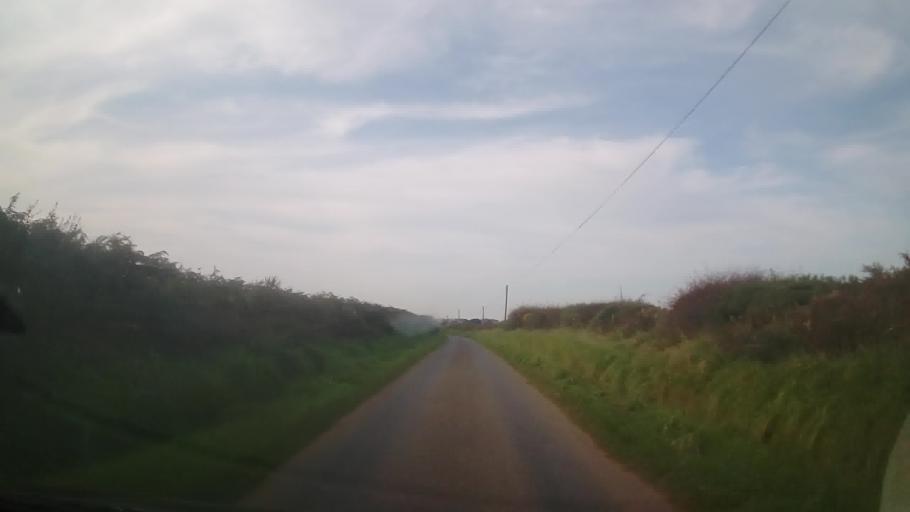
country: GB
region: Wales
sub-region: Pembrokeshire
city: Camrose
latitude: 51.8828
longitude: -5.0514
